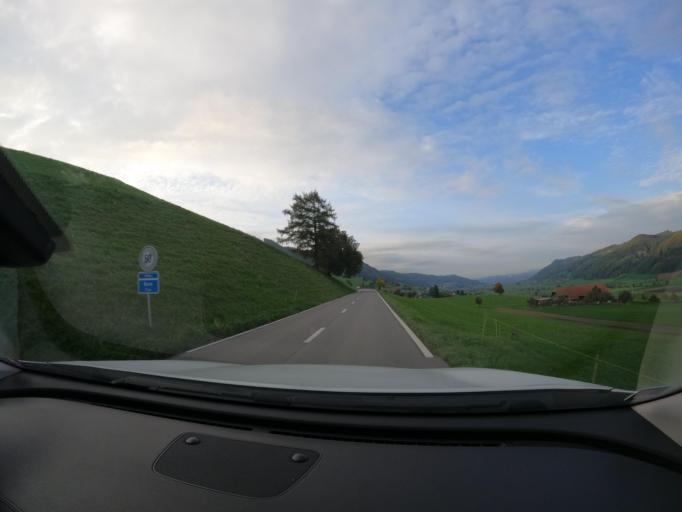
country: CH
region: Bern
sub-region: Bern-Mittelland District
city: Hermiswil
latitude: 46.8325
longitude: 7.4973
